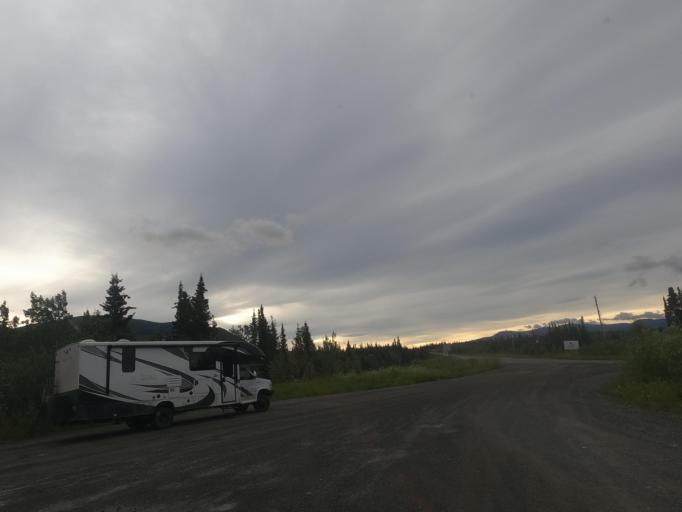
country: CA
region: Yukon
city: Haines Junction
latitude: 60.8589
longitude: -137.0606
